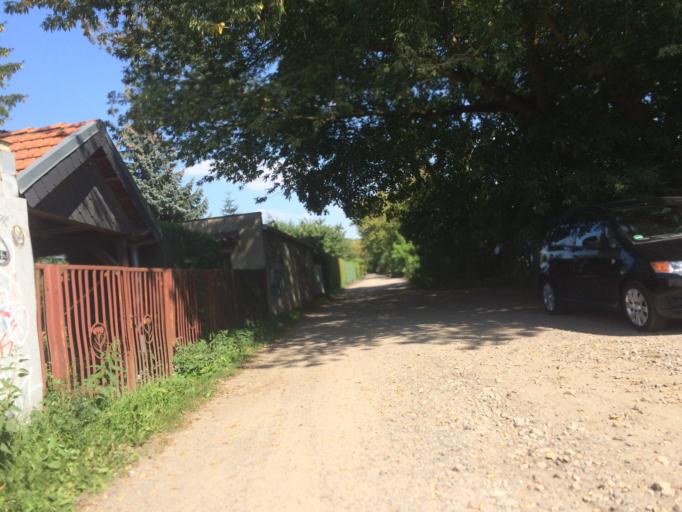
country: DE
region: Berlin
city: Niederschonhausen
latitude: 52.5928
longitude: 13.4135
